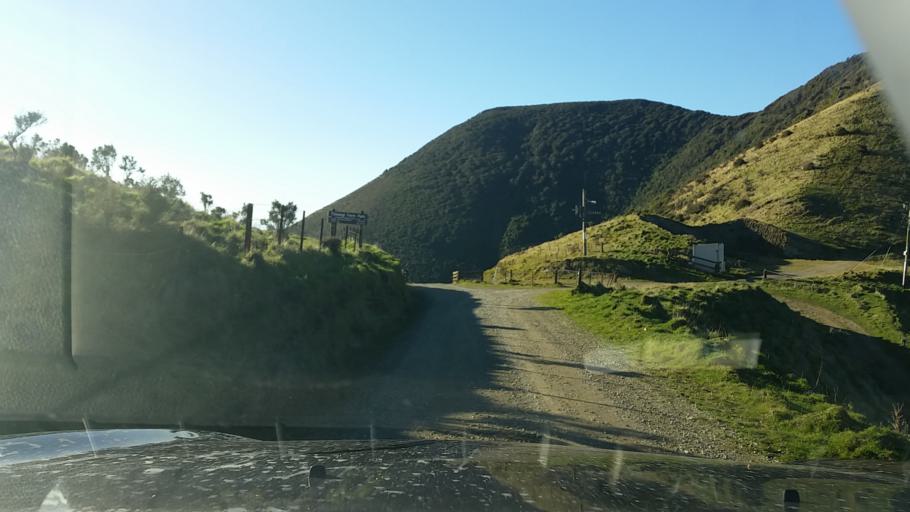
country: NZ
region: Marlborough
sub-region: Marlborough District
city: Picton
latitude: -41.0285
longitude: 174.1574
